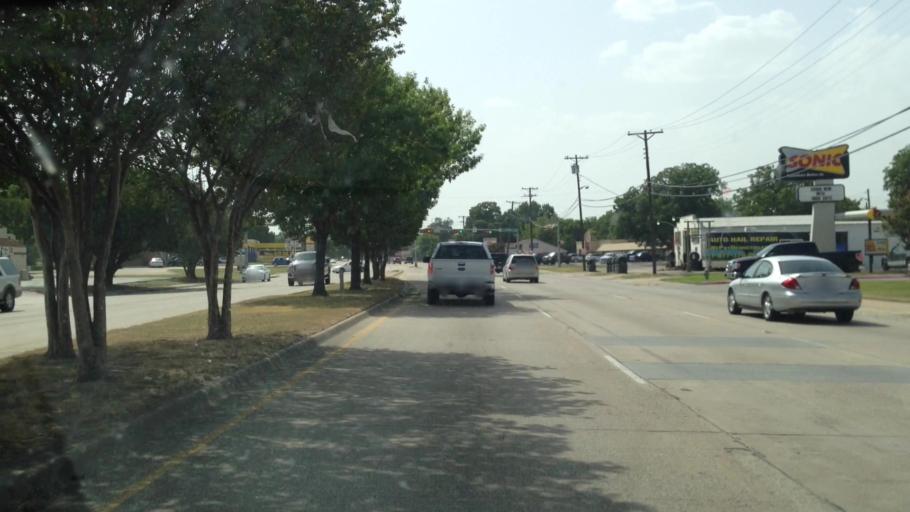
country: US
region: Texas
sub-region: Collin County
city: McKinney
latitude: 33.2148
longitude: -96.6189
